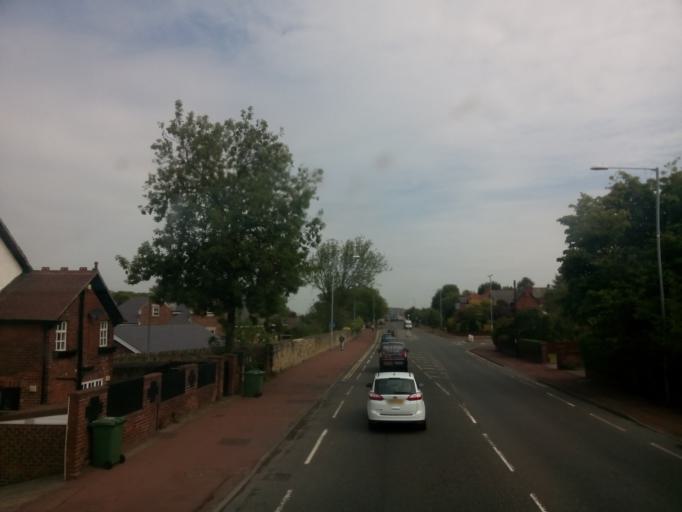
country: GB
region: England
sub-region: Gateshead
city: Gateshead
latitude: 54.9426
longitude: -1.5996
